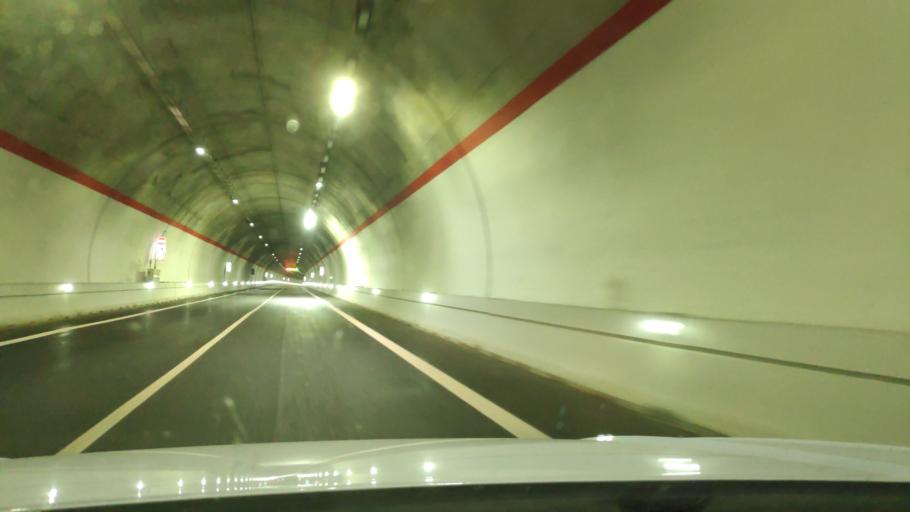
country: IT
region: Calabria
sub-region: Provincia di Reggio Calabria
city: Palizzi Marina
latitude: 37.9240
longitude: 15.9864
